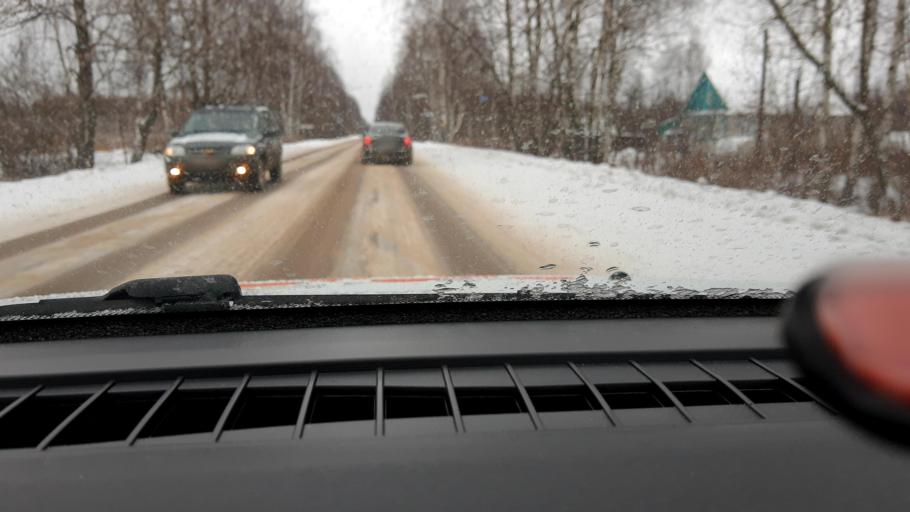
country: RU
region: Nizjnij Novgorod
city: Afonino
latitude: 56.3183
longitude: 44.1780
